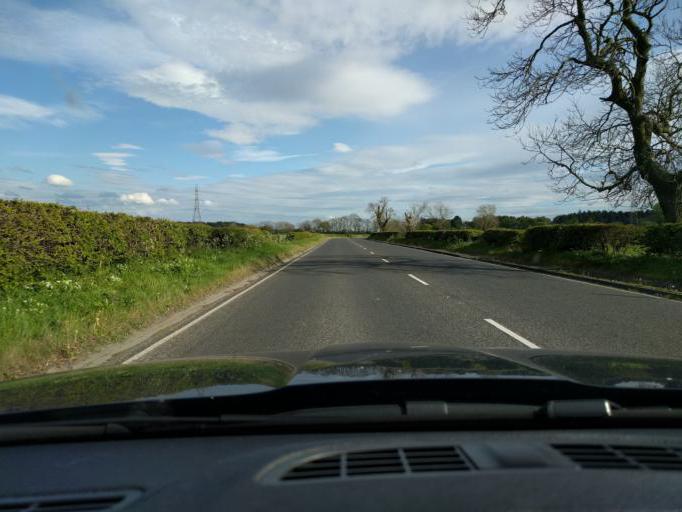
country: GB
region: England
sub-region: Northumberland
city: Stannington
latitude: 55.1408
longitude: -1.6522
